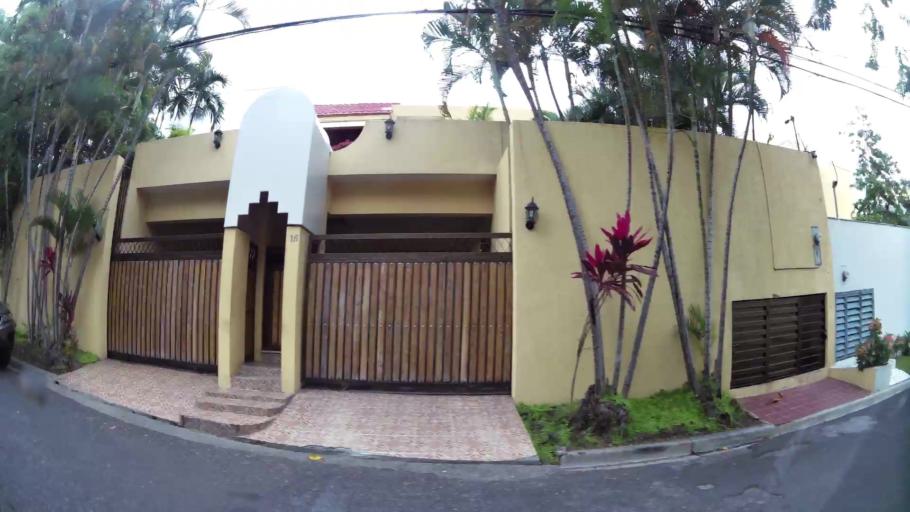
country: DO
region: Nacional
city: La Agustina
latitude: 18.4958
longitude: -69.9371
